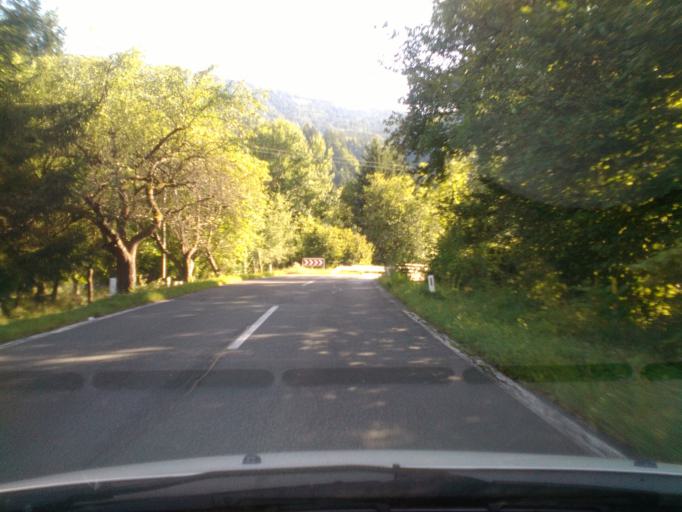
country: AT
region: Carinthia
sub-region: Politischer Bezirk Villach Land
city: Arnoldstein
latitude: 46.5427
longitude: 13.7754
